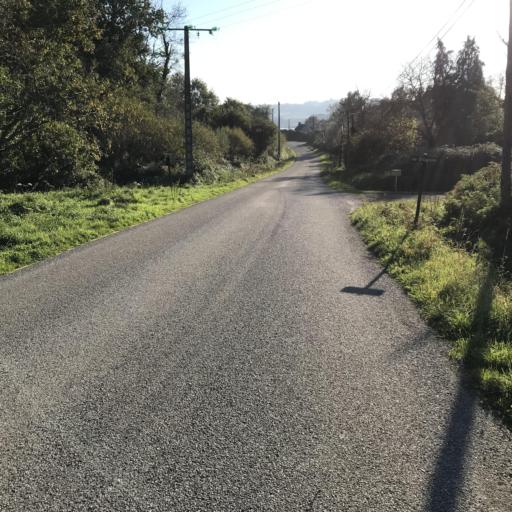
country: FR
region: Brittany
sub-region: Departement du Finistere
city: Hopital-Camfrout
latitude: 48.3037
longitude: -4.2335
